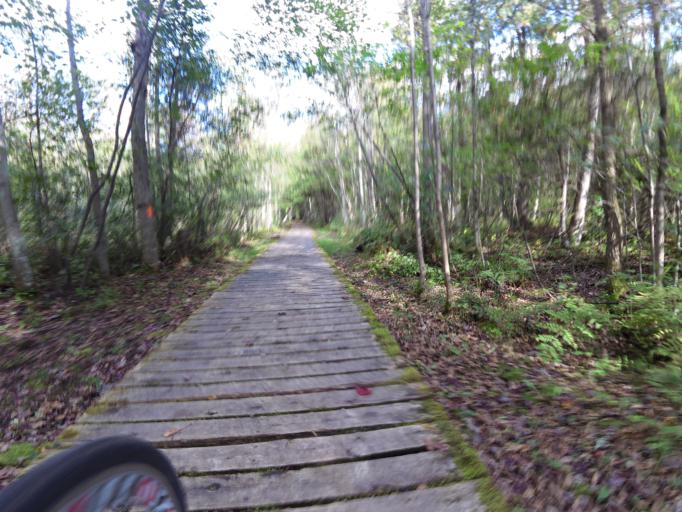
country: CA
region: Ontario
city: Bells Corners
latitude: 45.0971
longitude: -75.6318
